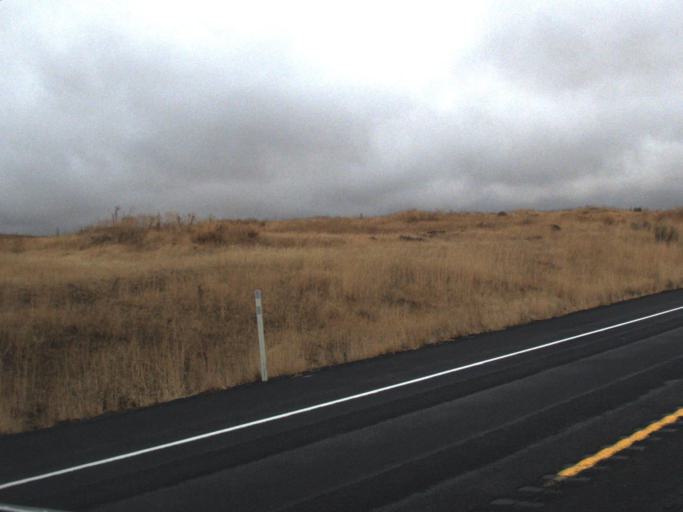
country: US
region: Washington
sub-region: Spokane County
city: Medical Lake
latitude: 47.6640
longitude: -117.8440
